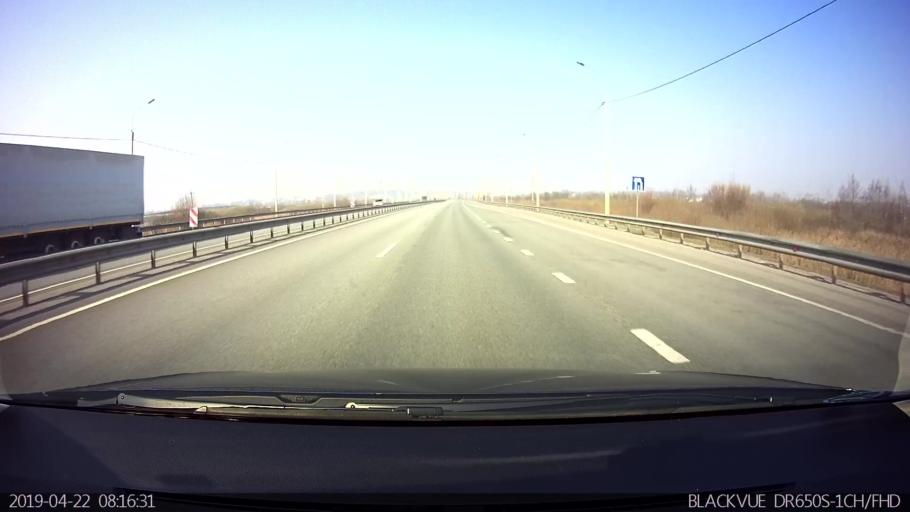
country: RU
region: Smolensk
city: Yartsevo
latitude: 55.0795
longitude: 32.6909
